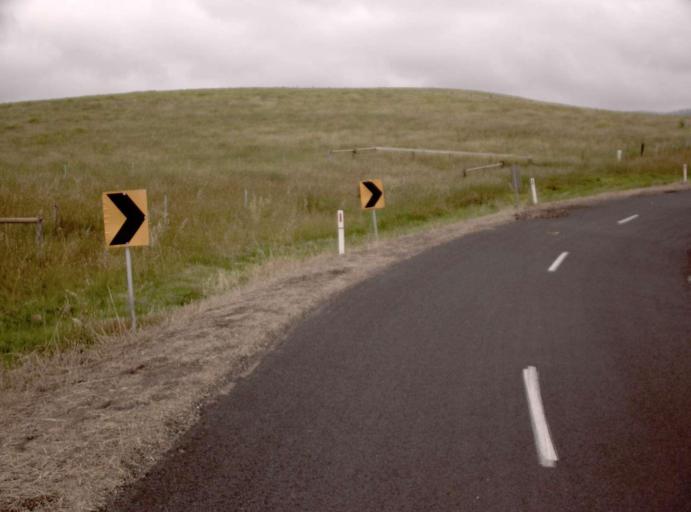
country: AU
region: Victoria
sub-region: Wellington
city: Heyfield
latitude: -37.8451
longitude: 146.7029
